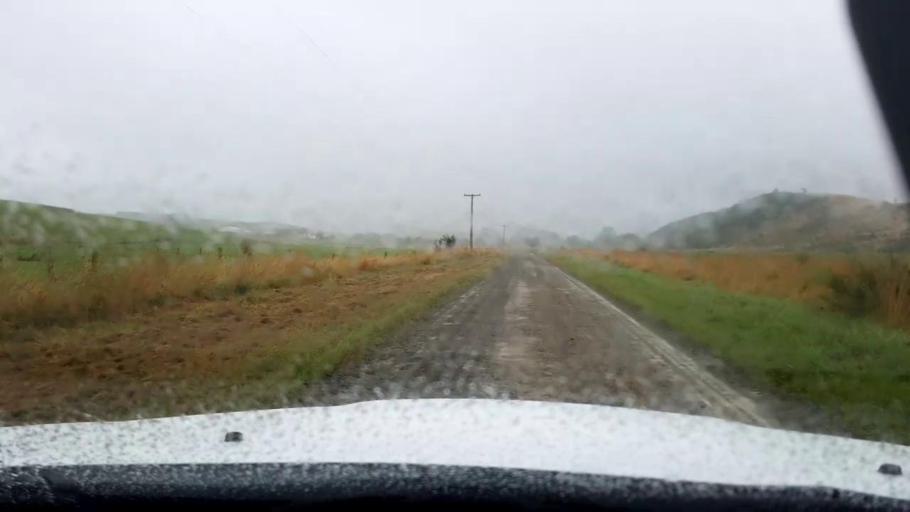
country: NZ
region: Canterbury
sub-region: Timaru District
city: Pleasant Point
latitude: -44.1667
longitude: 171.1901
